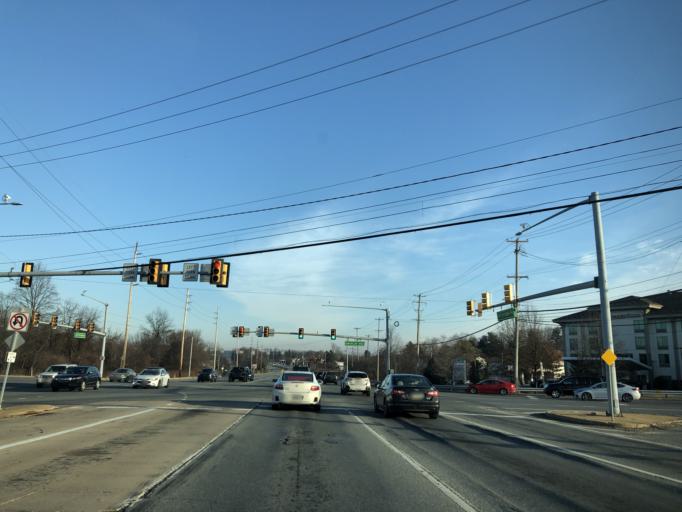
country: US
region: Pennsylvania
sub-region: Chester County
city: Exton
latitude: 40.0568
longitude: -75.6579
